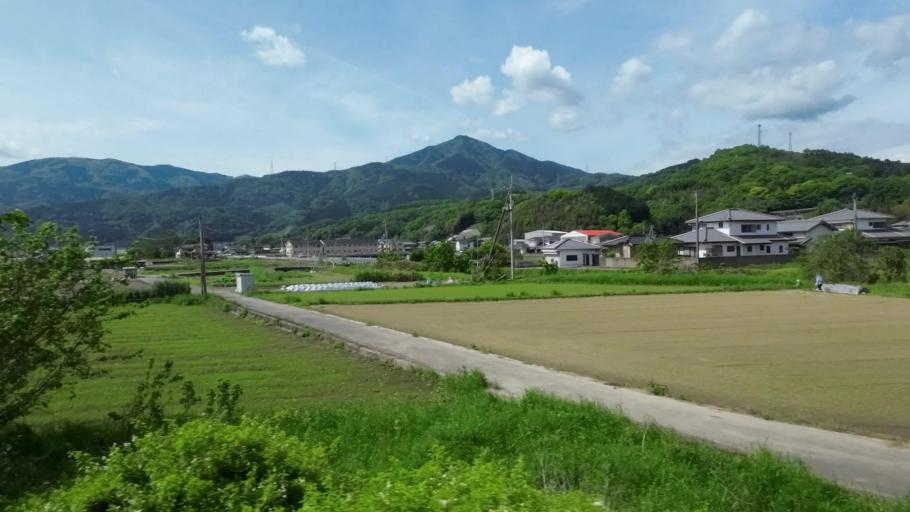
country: JP
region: Tokushima
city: Wakimachi
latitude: 34.0565
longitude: 134.2234
